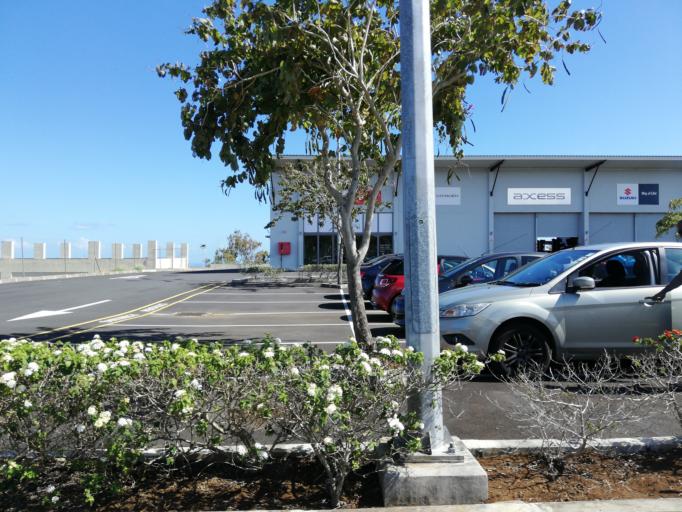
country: MU
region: Moka
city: Moka
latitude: -20.2273
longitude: 57.4915
